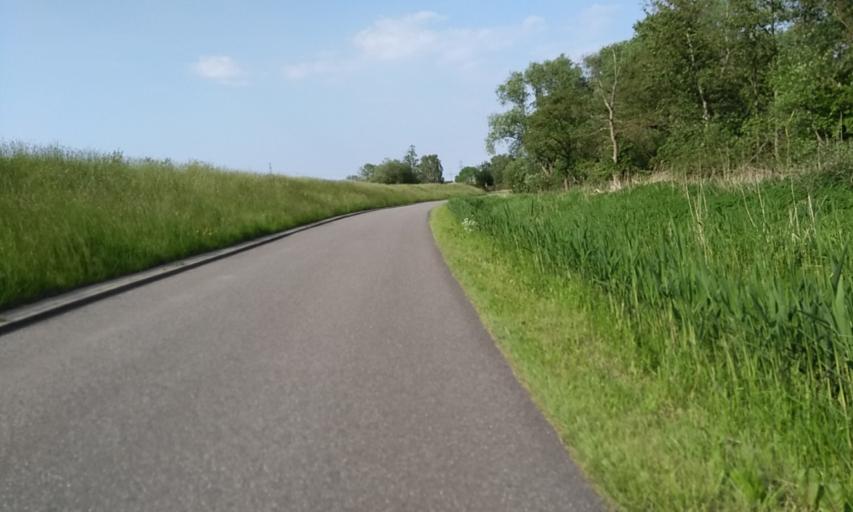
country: DE
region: Lower Saxony
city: Buxtehude
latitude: 53.4829
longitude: 9.7074
